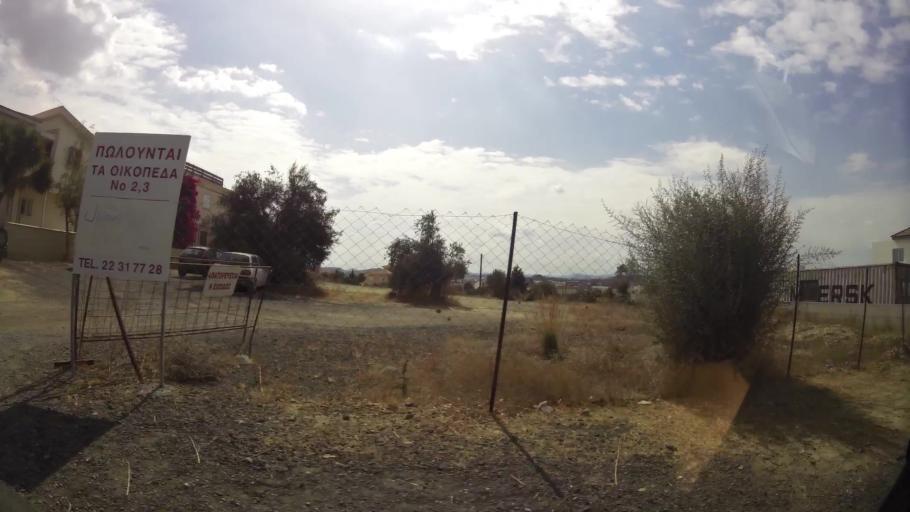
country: CY
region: Lefkosia
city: Tseri
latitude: 35.0721
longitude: 33.3286
